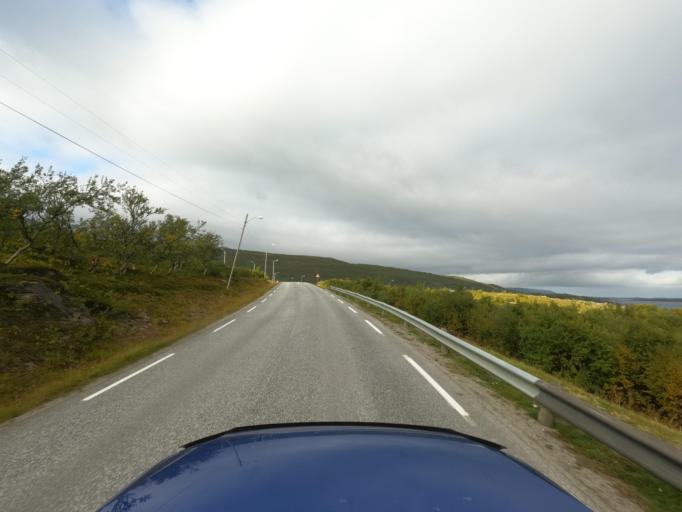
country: NO
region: Finnmark Fylke
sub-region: Porsanger
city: Lakselv
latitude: 70.3127
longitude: 25.0525
